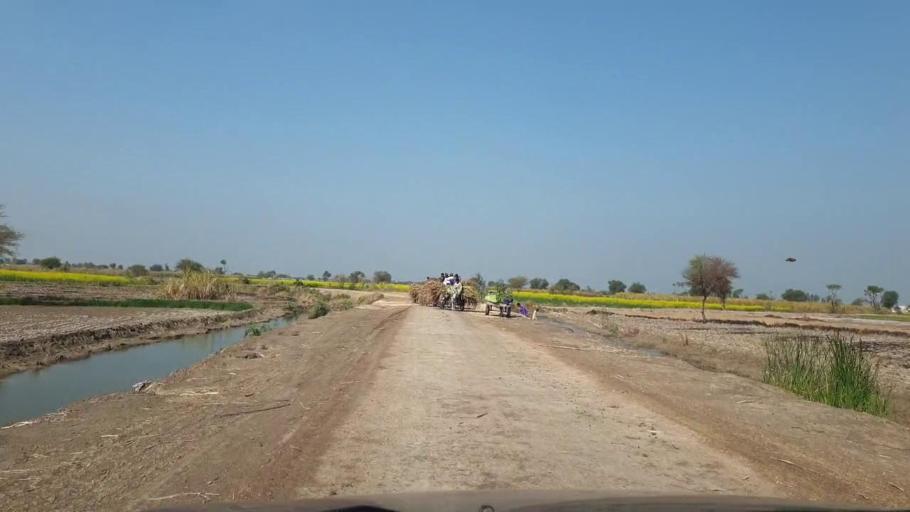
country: PK
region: Sindh
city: Sinjhoro
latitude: 26.0473
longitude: 68.7379
